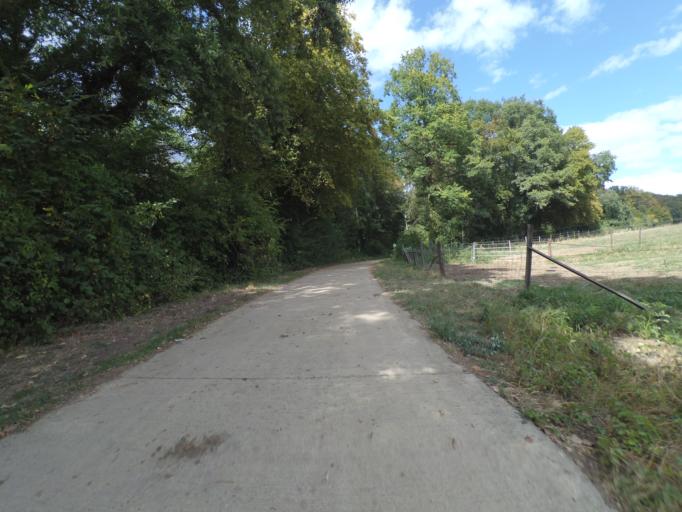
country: LU
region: Grevenmacher
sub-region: Canton de Remich
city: Mondorf-les-Bains
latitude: 49.5213
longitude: 6.3110
